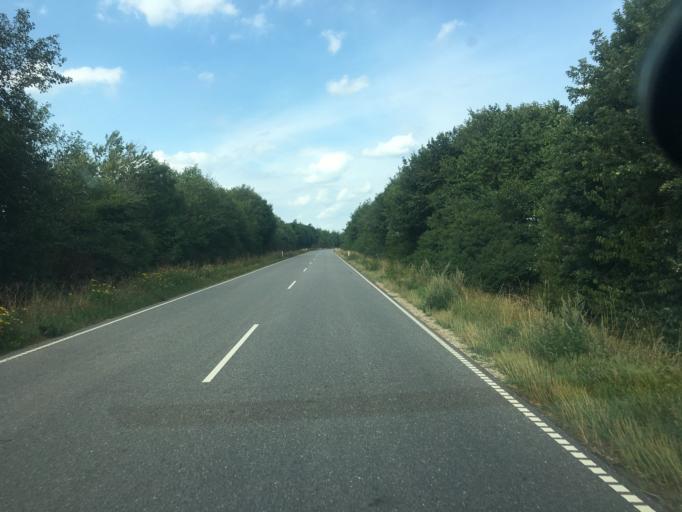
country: DK
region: South Denmark
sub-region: Aabenraa Kommune
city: Tinglev
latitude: 54.9392
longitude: 9.3029
